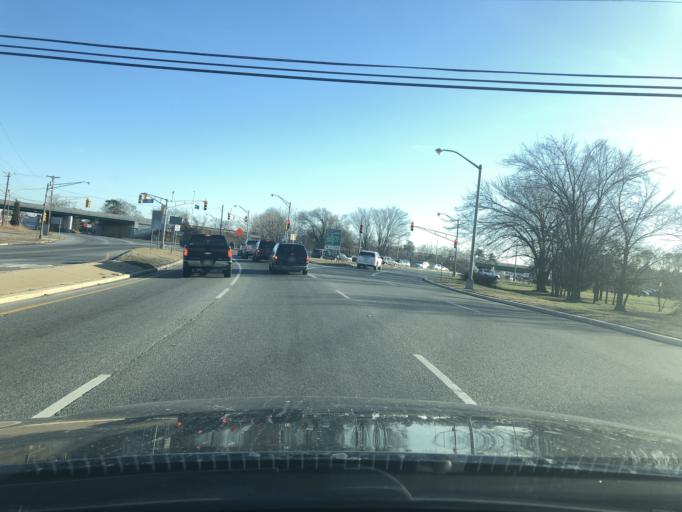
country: US
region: New Jersey
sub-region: Atlantic County
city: Northfield
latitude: 39.4011
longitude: -74.5618
